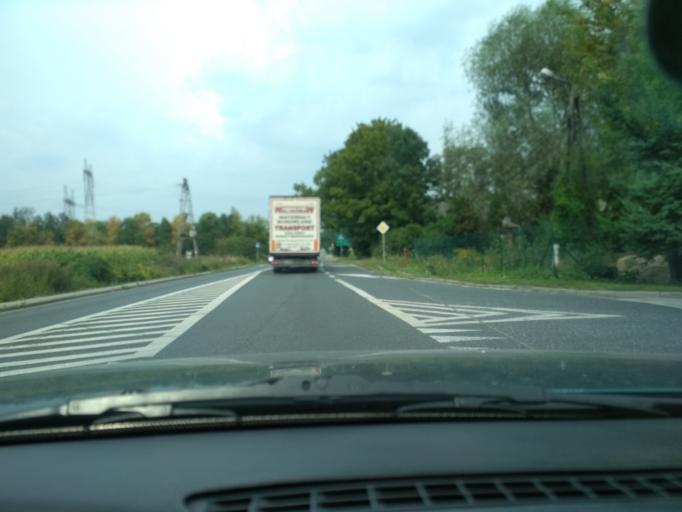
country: PL
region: Silesian Voivodeship
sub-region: Powiat bierunsko-ledzinski
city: Chelm Slaski
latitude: 50.0862
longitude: 19.1998
